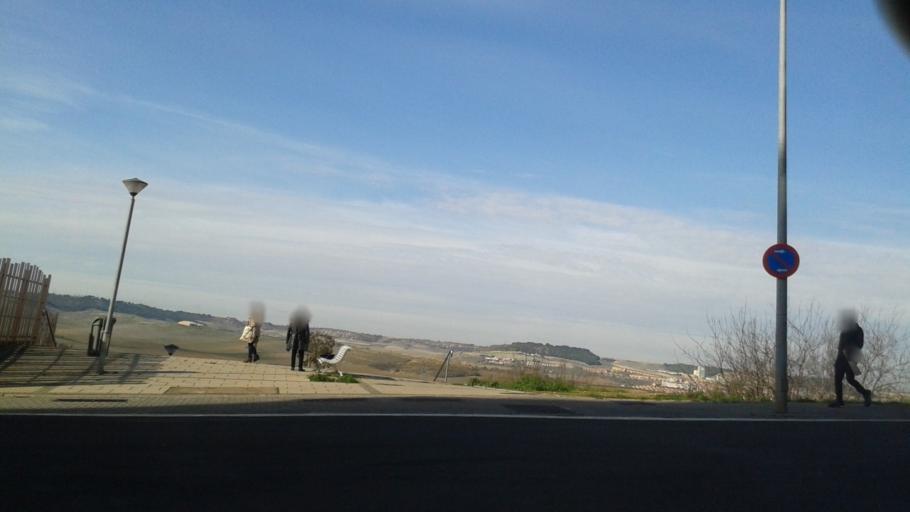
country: ES
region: Castille and Leon
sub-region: Provincia de Valladolid
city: Zaratan
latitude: 41.6367
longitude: -4.7690
